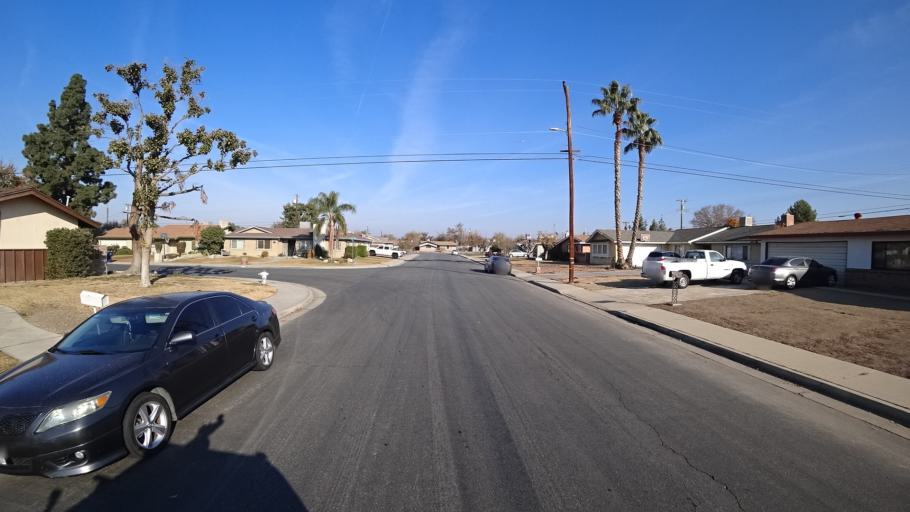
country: US
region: California
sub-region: Kern County
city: Greenfield
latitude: 35.3157
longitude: -119.0130
